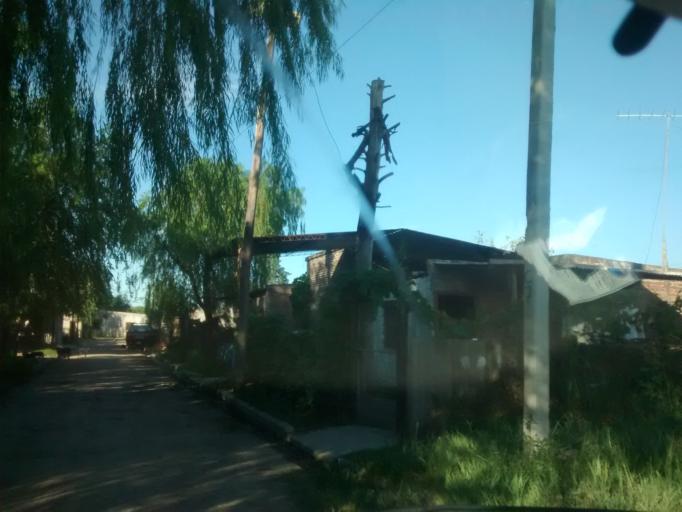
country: AR
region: Chaco
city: Fontana
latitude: -27.4551
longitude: -59.0275
